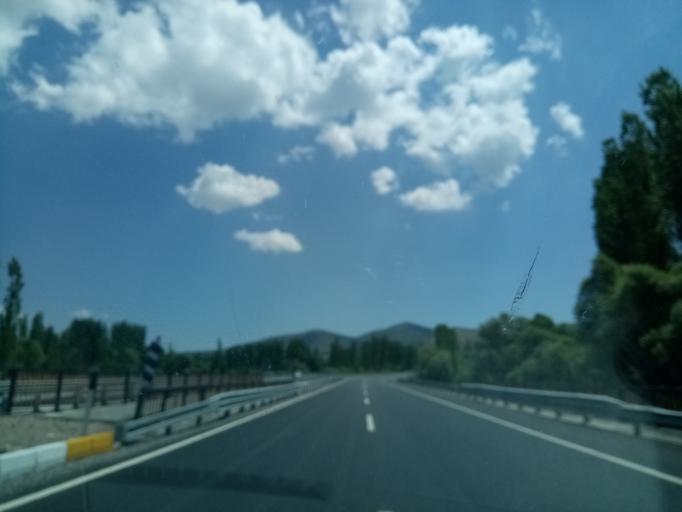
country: TR
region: Konya
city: Cavus
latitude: 37.6608
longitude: 31.9819
